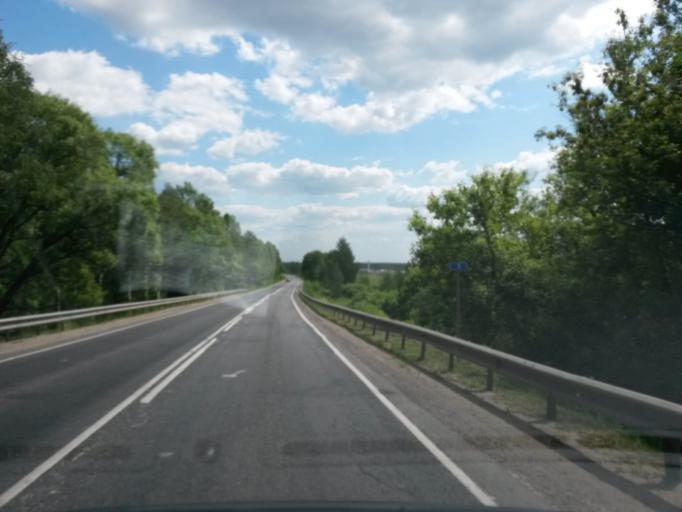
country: RU
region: Jaroslavl
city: Yaroslavl
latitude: 57.5547
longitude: 39.8760
